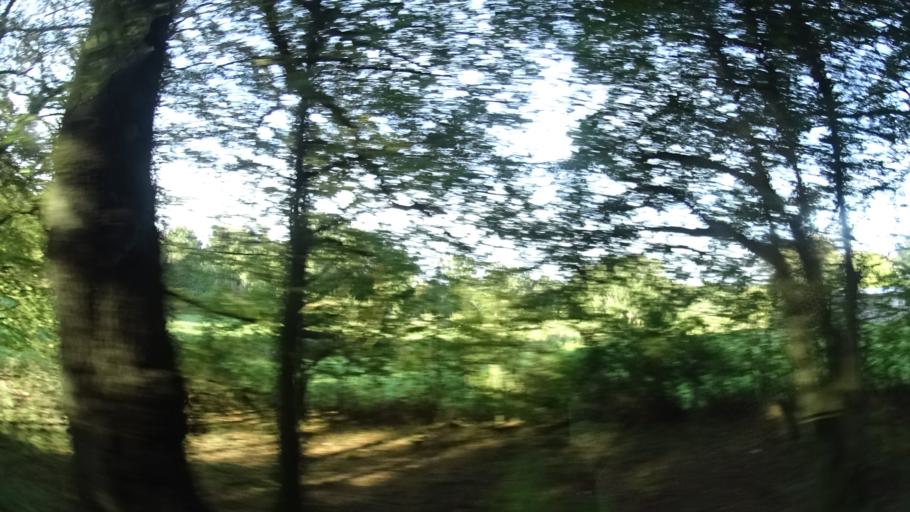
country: DE
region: Hesse
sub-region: Regierungsbezirk Darmstadt
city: Wachtersbach
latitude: 50.2889
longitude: 9.2497
